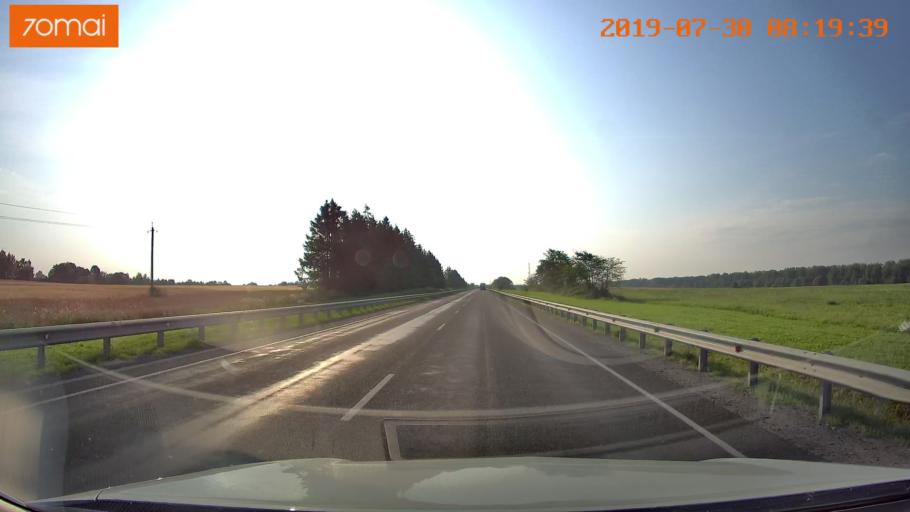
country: RU
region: Kaliningrad
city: Chernyakhovsk
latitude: 54.6276
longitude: 21.4973
